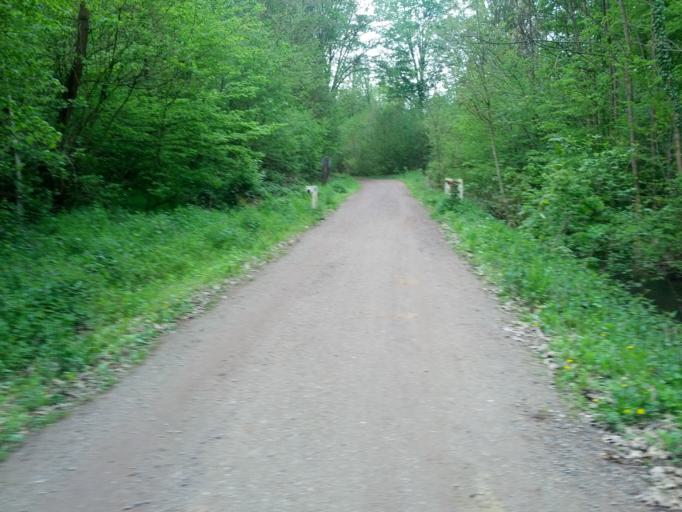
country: DE
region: Baden-Wuerttemberg
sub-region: Freiburg Region
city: Umkirch
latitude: 48.0122
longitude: 7.7618
